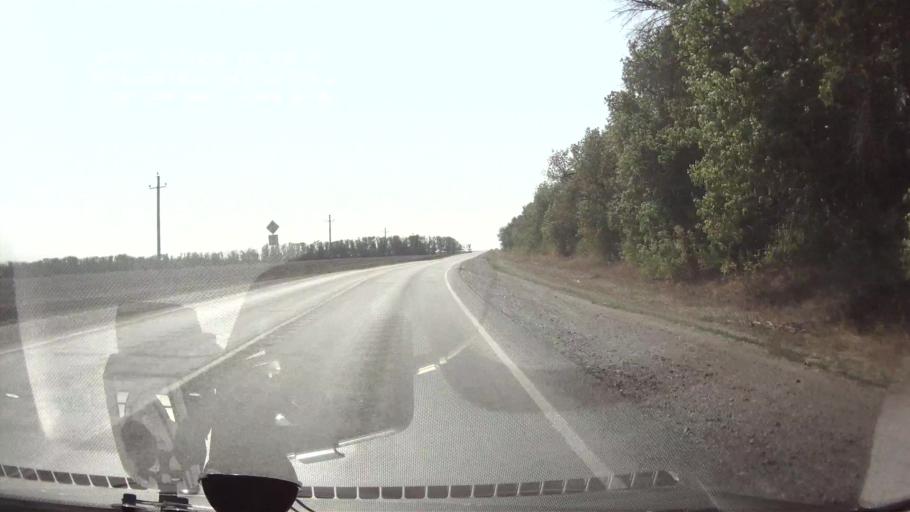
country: RU
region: Krasnodarskiy
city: Dmitriyevskaya
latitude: 45.6972
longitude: 40.7442
